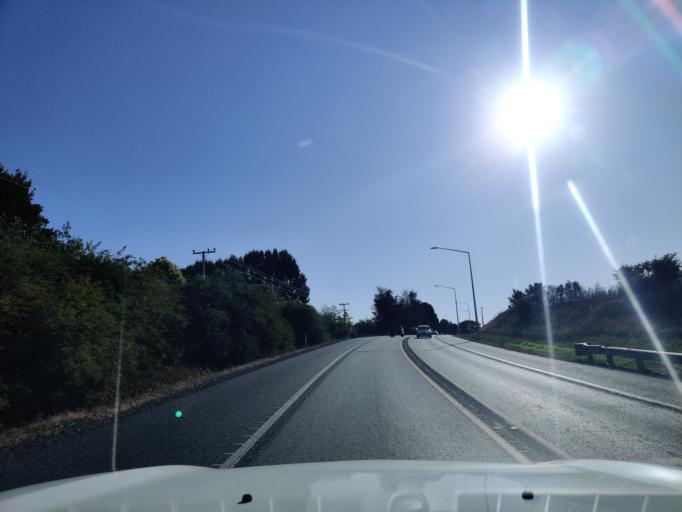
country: NZ
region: Auckland
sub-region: Auckland
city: Papakura
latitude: -37.1241
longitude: 174.9168
